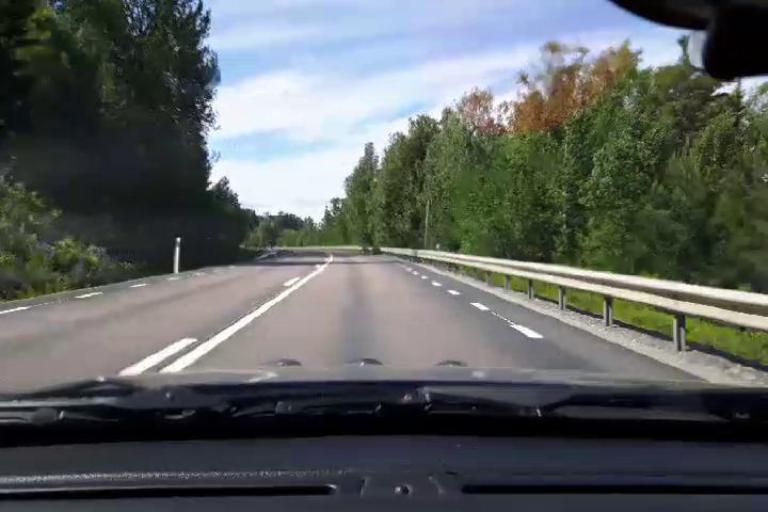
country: SE
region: Gaevleborg
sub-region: Bollnas Kommun
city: Kilafors
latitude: 61.1901
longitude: 16.7731
